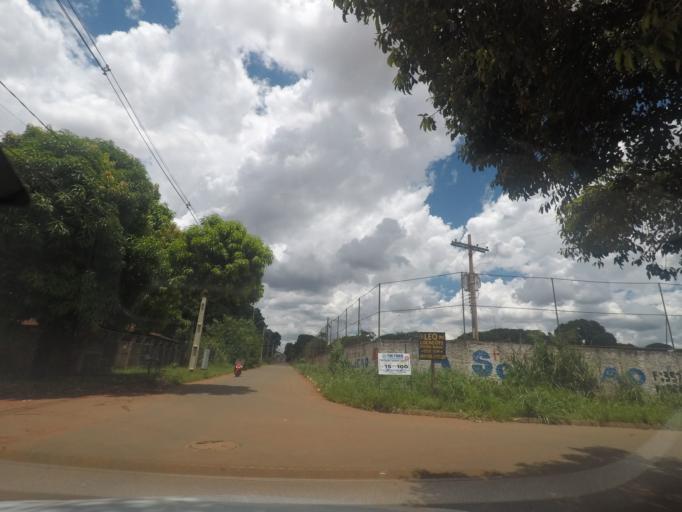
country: BR
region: Goias
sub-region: Goiania
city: Goiania
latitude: -16.7076
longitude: -49.3478
